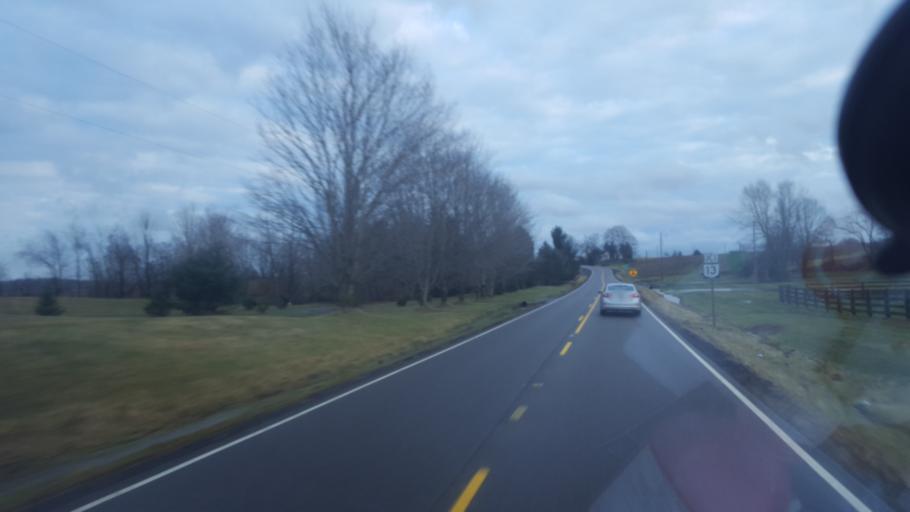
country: US
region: Ohio
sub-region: Knox County
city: Fredericktown
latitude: 40.5264
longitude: -82.5506
